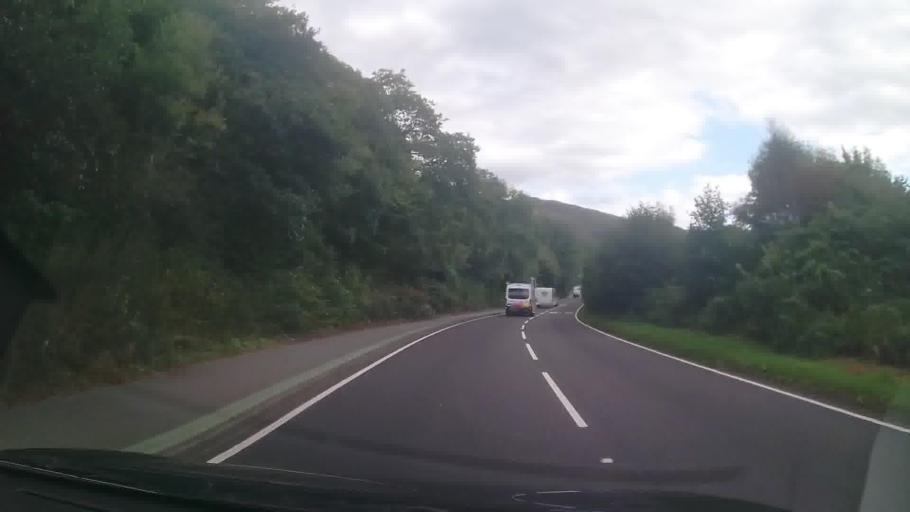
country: GB
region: Scotland
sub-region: Highland
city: Fort William
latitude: 56.7009
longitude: -5.1905
